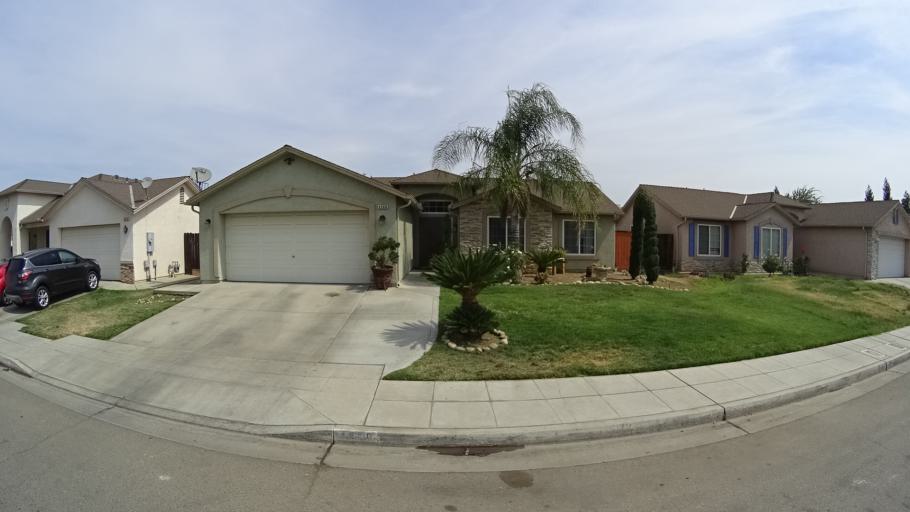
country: US
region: California
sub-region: Fresno County
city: West Park
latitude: 36.7613
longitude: -119.8749
